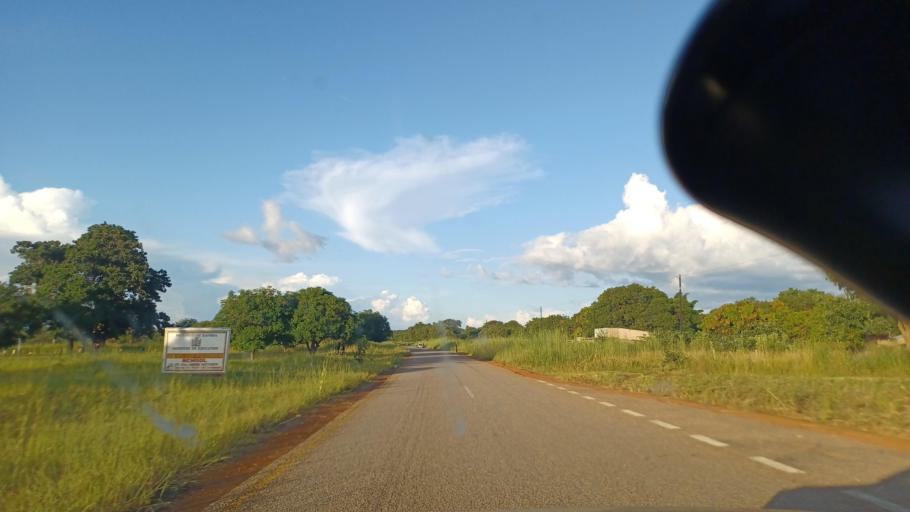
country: ZM
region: North-Western
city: Kalengwa
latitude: -13.1329
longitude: 25.1686
